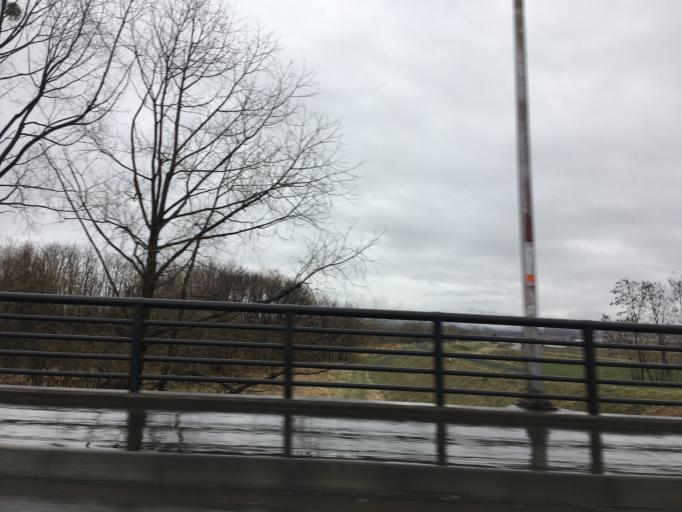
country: JP
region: Hokkaido
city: Nayoro
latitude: 44.1269
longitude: 142.4841
